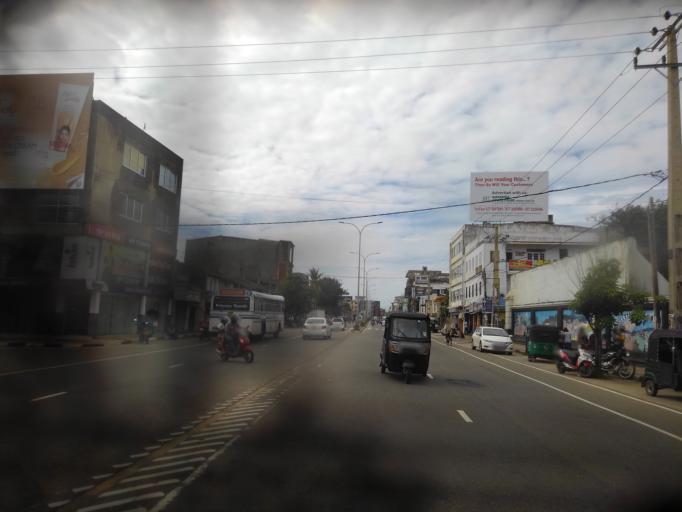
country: LK
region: Southern
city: Galle
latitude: 6.0338
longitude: 80.2130
